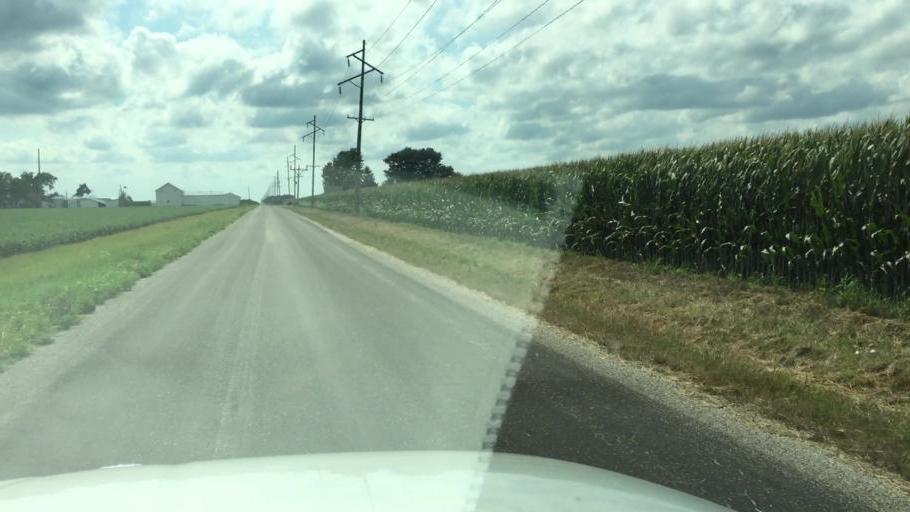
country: US
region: Illinois
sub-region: Hancock County
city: Carthage
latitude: 40.4169
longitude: -91.1744
